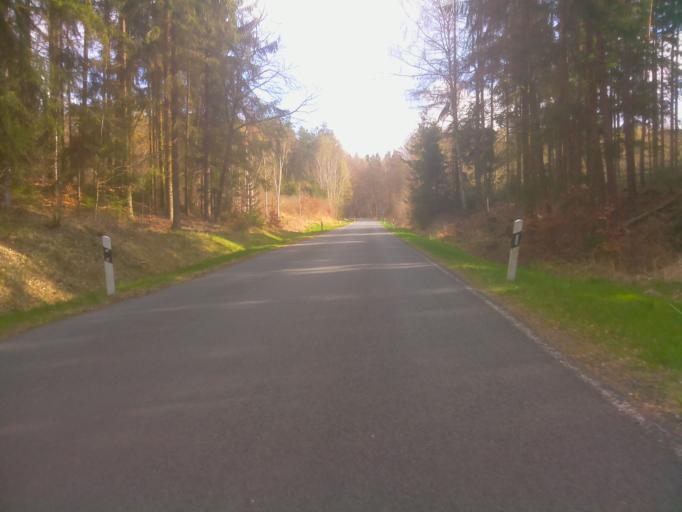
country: DE
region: Thuringia
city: Lindig
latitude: 50.7658
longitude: 11.6025
